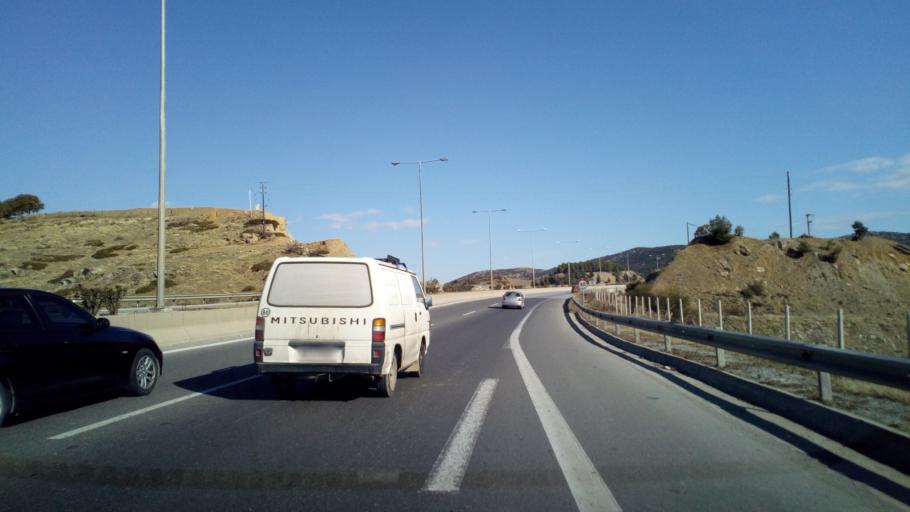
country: GR
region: Central Macedonia
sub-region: Nomos Thessalonikis
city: Efkarpia
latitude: 40.6863
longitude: 22.9586
